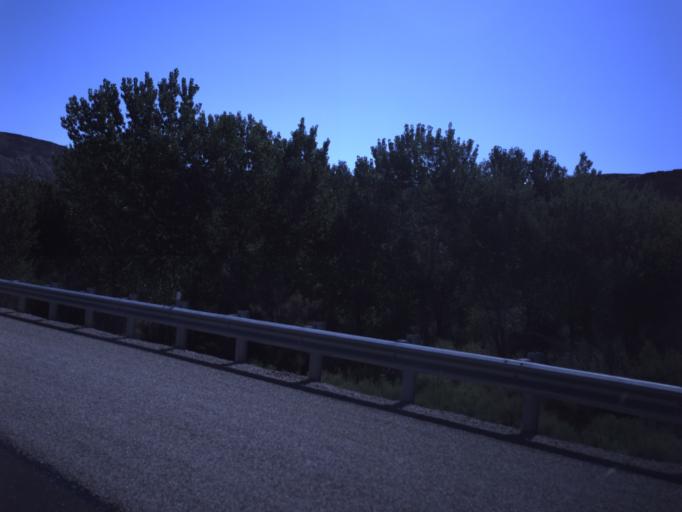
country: US
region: Utah
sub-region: Wayne County
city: Loa
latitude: 38.2933
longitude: -111.0445
